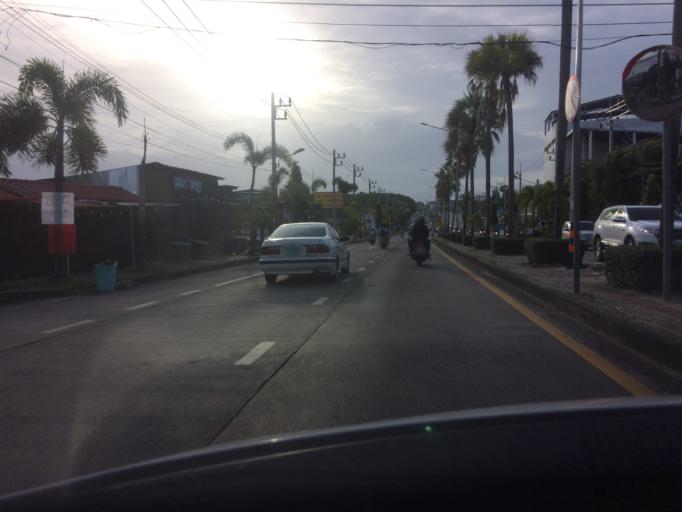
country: TH
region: Phuket
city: Ban Talat Nua
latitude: 7.8688
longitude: 98.3824
